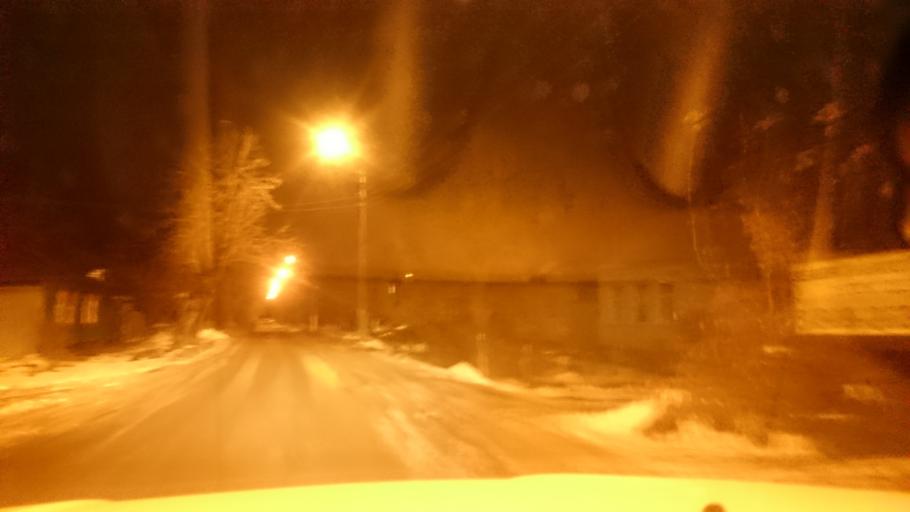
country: RU
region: Tula
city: Tula
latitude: 54.1863
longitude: 37.6322
